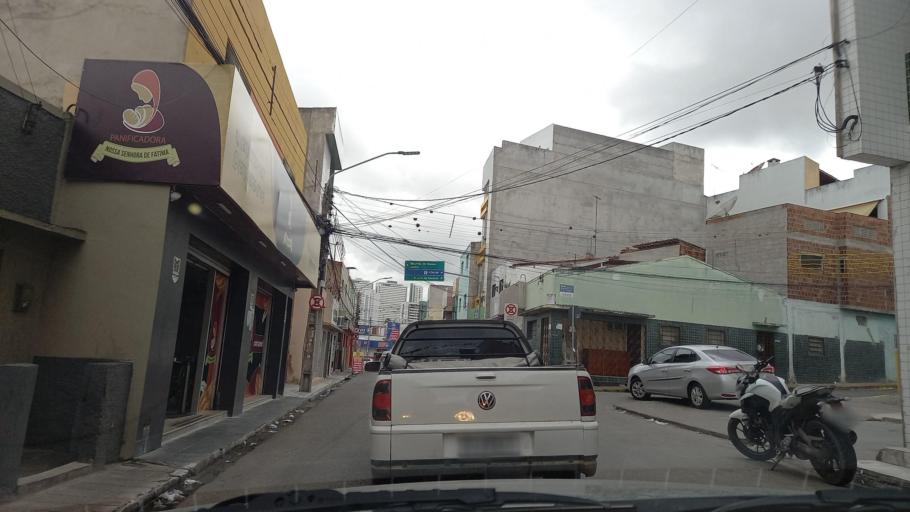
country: BR
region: Pernambuco
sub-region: Caruaru
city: Caruaru
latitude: -8.2757
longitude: -35.9656
